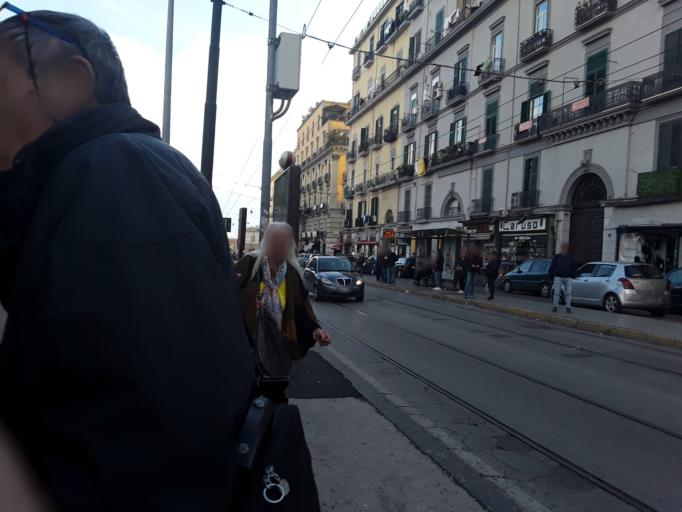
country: IT
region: Campania
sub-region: Provincia di Napoli
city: Napoli
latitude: 40.8492
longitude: 14.2687
